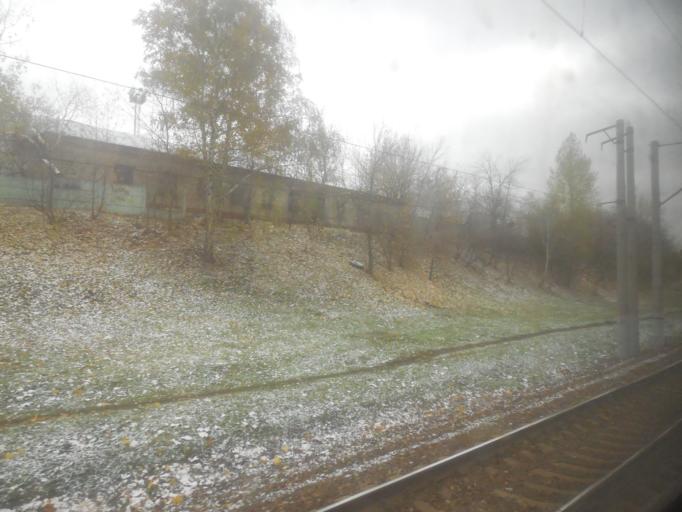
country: RU
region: Moskovskaya
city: Presnenskiy
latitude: 55.7710
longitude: 37.5390
